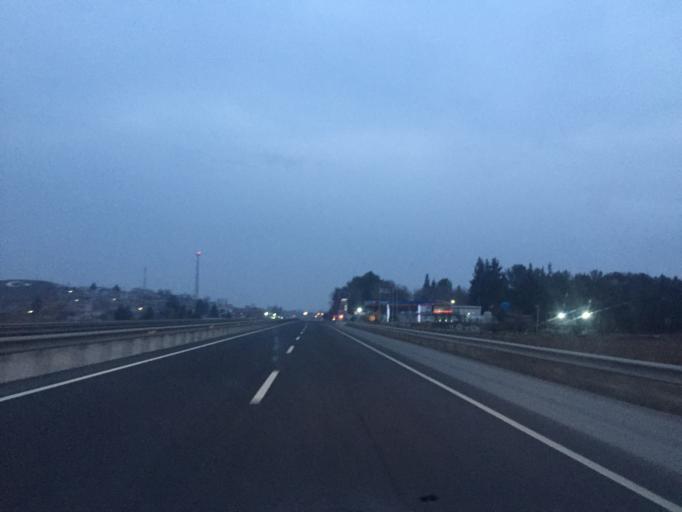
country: TR
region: Sanliurfa
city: Camlidere
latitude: 37.1550
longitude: 39.0588
